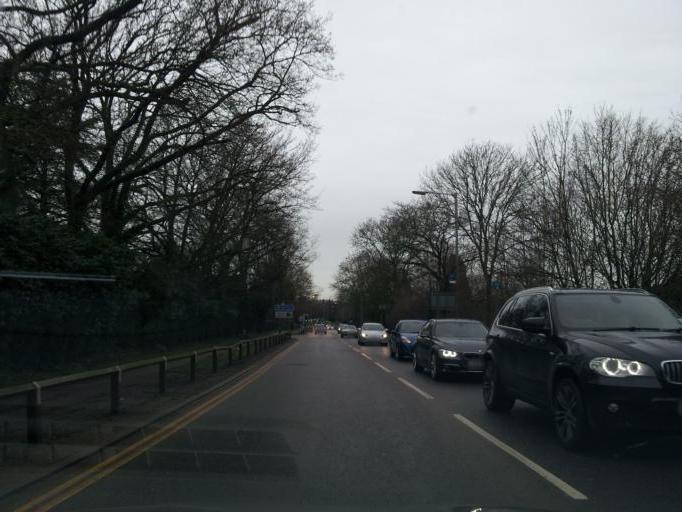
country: GB
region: England
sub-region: Cambridgeshire
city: Cambridge
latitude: 52.1745
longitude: 0.1484
